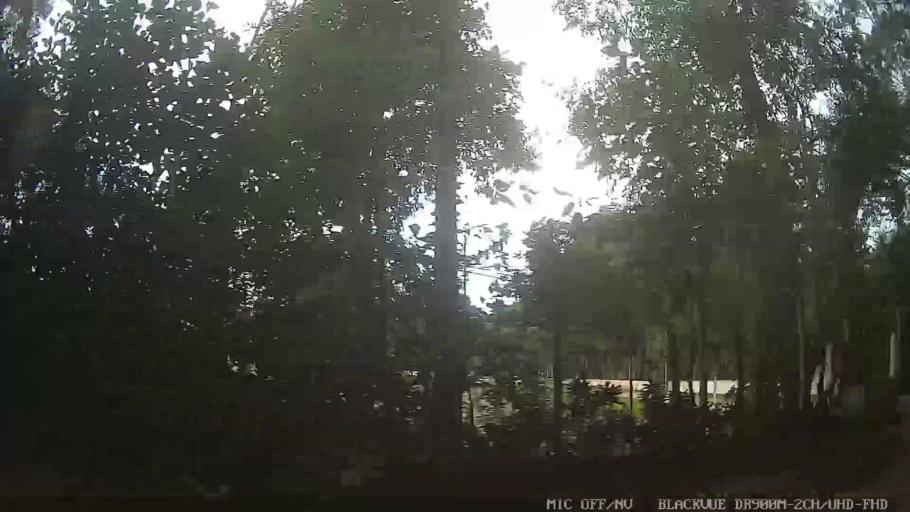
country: BR
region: Sao Paulo
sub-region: Bom Jesus Dos Perdoes
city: Bom Jesus dos Perdoes
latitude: -23.1263
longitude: -46.4948
